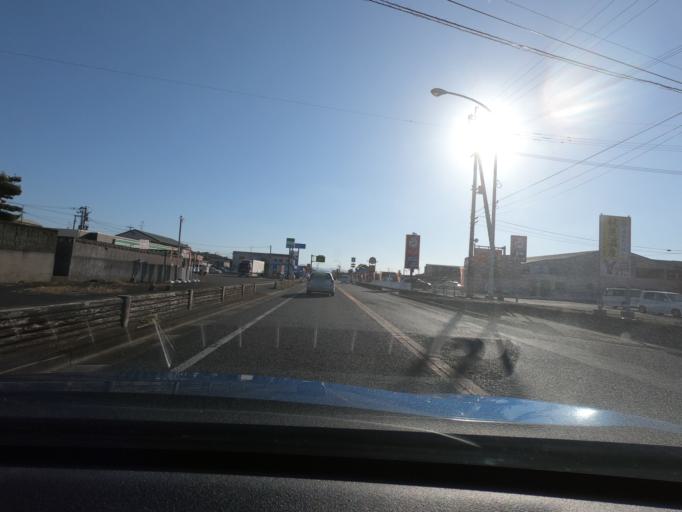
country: JP
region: Kagoshima
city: Izumi
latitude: 32.1263
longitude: 130.3433
